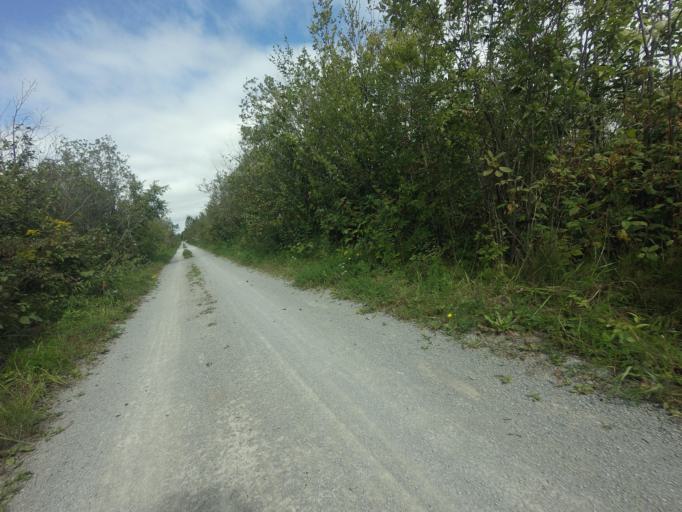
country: CA
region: Ontario
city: Uxbridge
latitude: 44.1795
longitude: -79.0714
